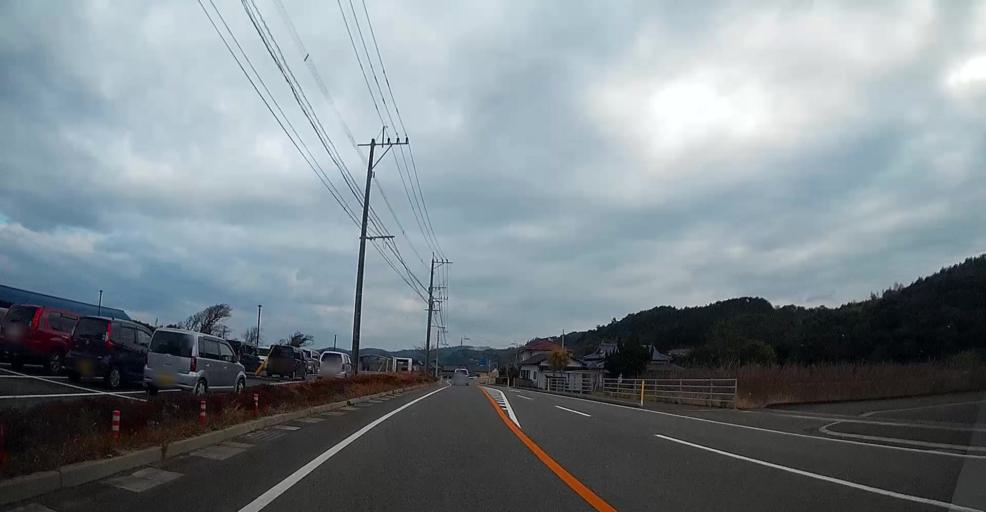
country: JP
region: Kumamoto
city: Hondo
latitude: 32.4828
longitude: 130.2753
